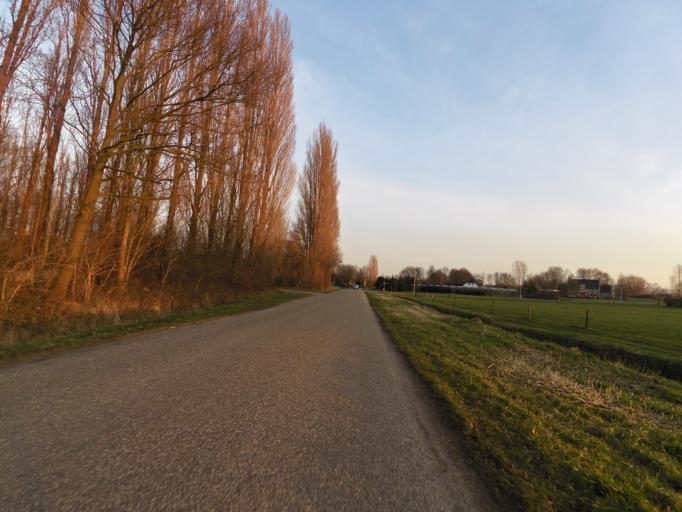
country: NL
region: Gelderland
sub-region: Gemeente Zevenaar
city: Zevenaar
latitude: 51.9438
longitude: 6.1165
